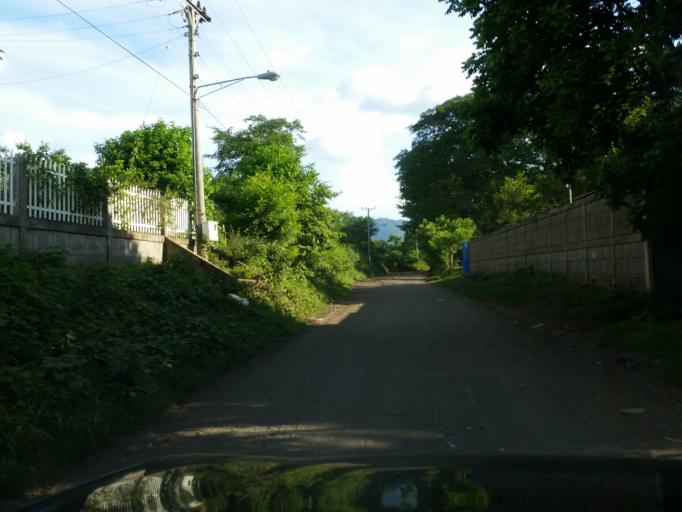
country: NI
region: Managua
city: Managua
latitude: 12.0869
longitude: -86.2073
